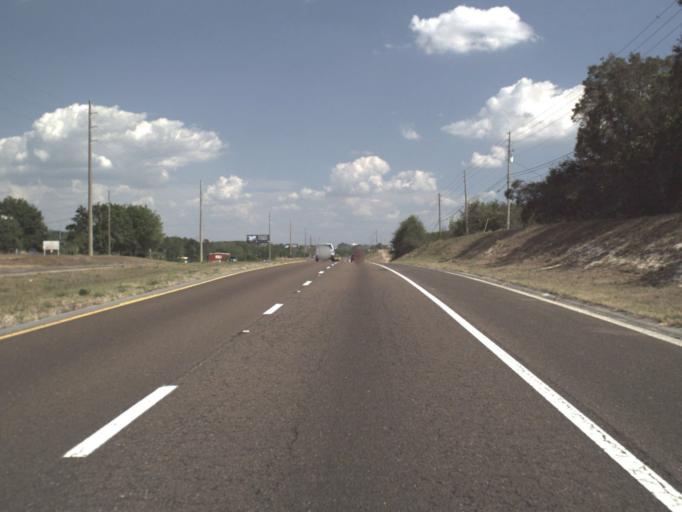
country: US
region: Florida
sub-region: Lake County
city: Minneola
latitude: 28.6319
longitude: -81.7749
